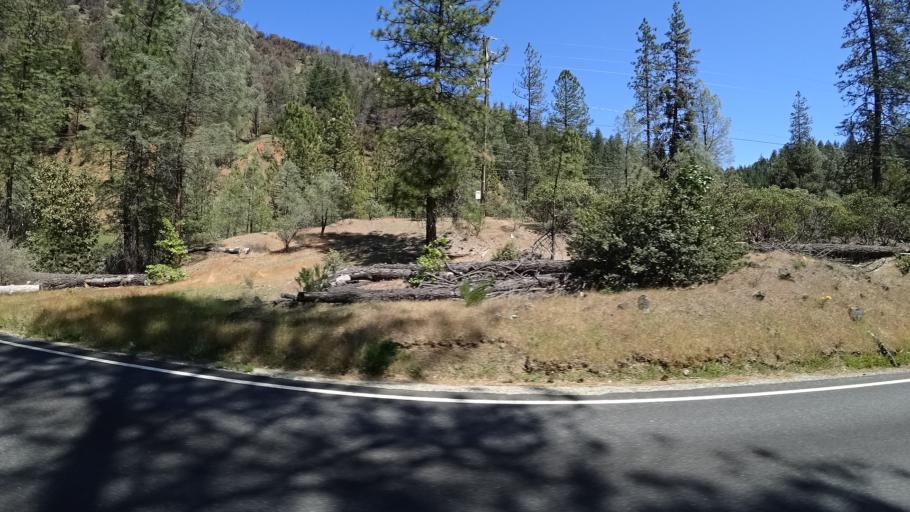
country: US
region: California
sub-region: Trinity County
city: Weaverville
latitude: 40.7572
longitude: -123.0665
